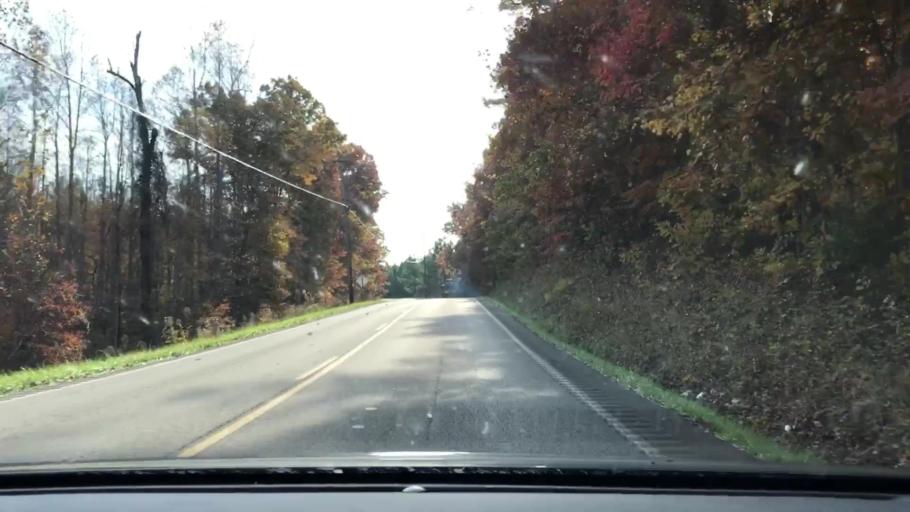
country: US
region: Tennessee
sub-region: Scott County
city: Huntsville
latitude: 36.3410
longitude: -84.6481
